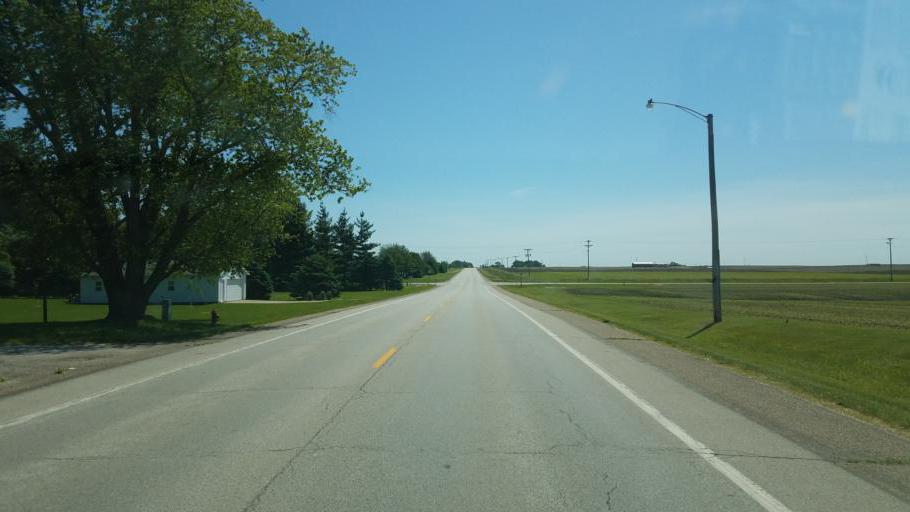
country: US
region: Illinois
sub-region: McLean County
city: Heyworth
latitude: 40.3121
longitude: -88.9708
